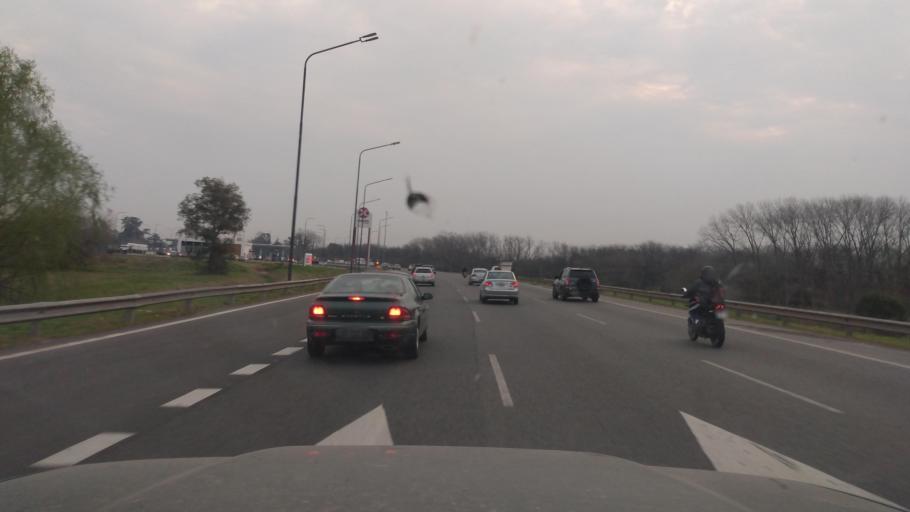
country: AR
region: Buenos Aires
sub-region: Partido de Merlo
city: Merlo
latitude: -34.6031
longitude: -58.7067
